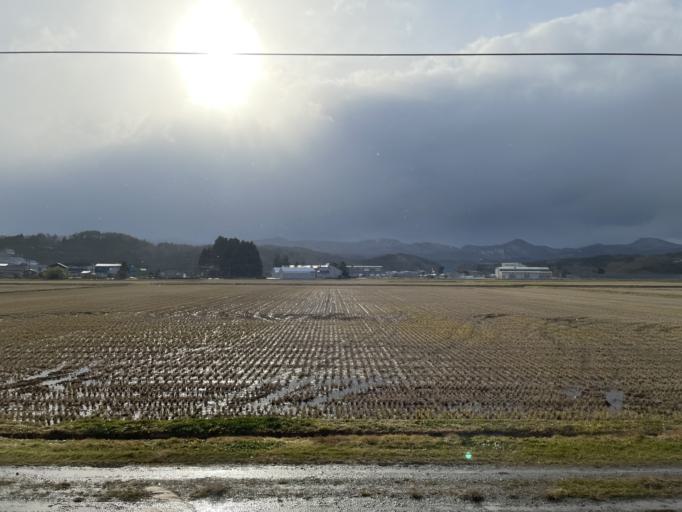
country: JP
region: Aomori
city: Aomori Shi
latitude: 41.0542
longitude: 140.5922
